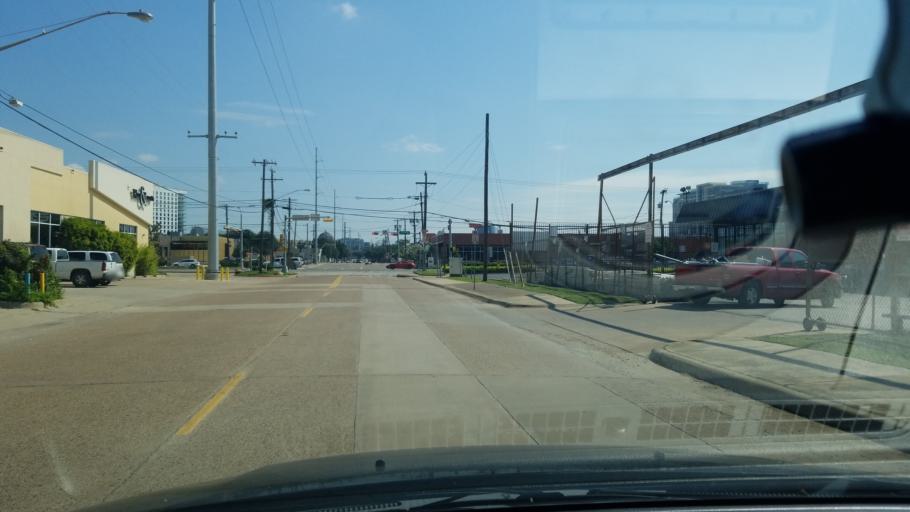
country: US
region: Texas
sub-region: Dallas County
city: Dallas
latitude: 32.7916
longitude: -96.8237
